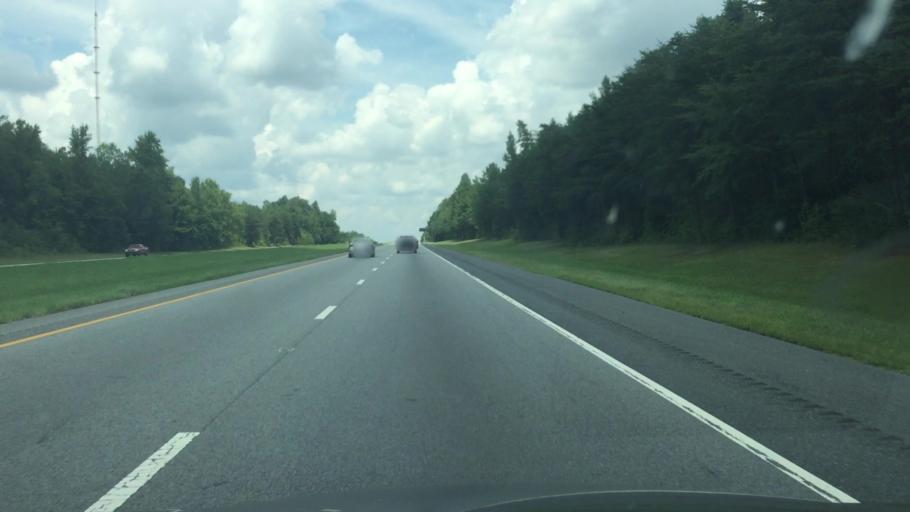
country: US
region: North Carolina
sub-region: Guilford County
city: Pleasant Garden
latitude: 35.9596
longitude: -79.8201
